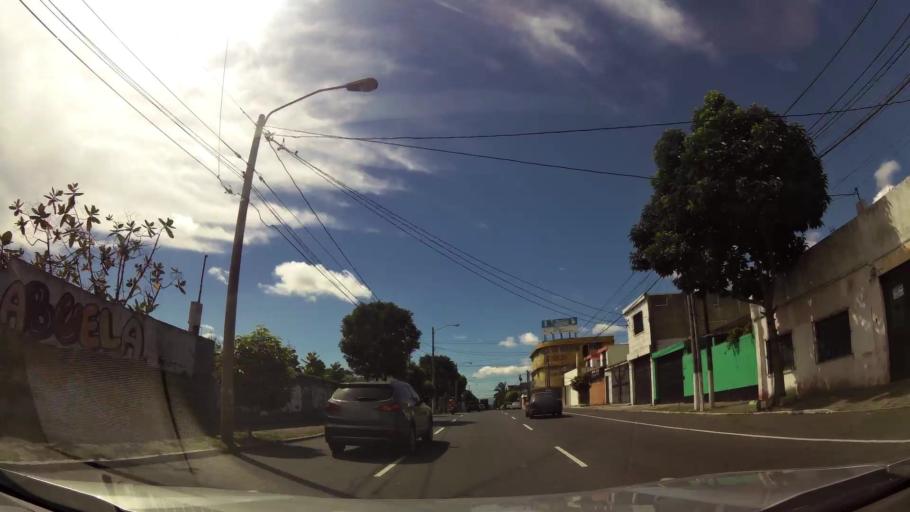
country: GT
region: Guatemala
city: Guatemala City
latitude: 14.6027
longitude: -90.5438
